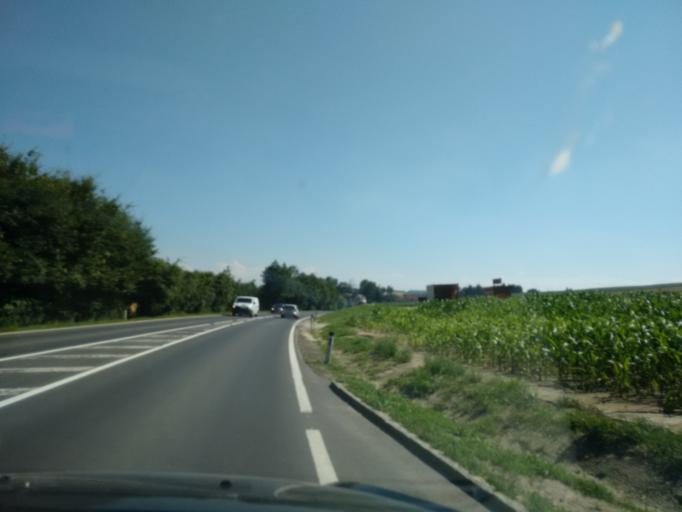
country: AT
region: Upper Austria
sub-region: Politischer Bezirk Grieskirchen
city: Bad Schallerbach
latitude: 48.2306
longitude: 13.9667
